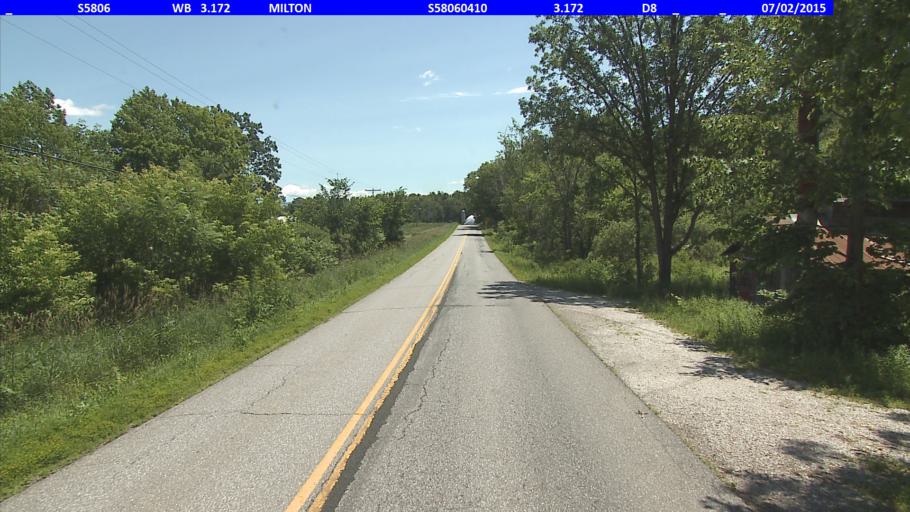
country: US
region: Vermont
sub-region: Chittenden County
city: Milton
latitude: 44.6696
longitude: -73.1701
